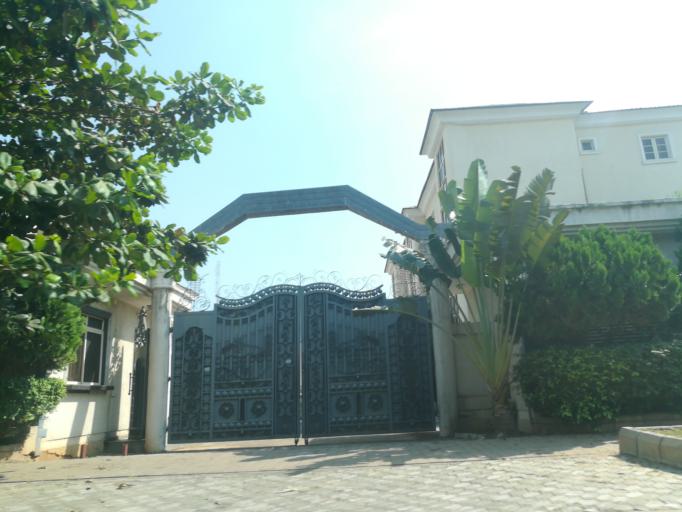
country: NG
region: Abuja Federal Capital Territory
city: Abuja
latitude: 9.0612
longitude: 7.4258
